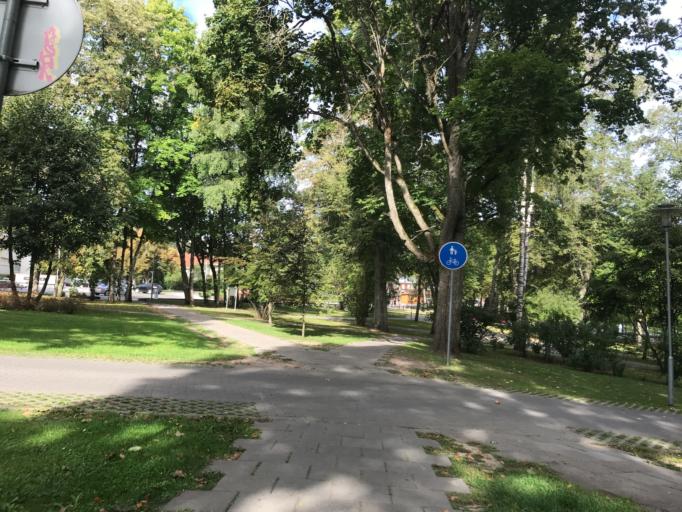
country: LT
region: Alytaus apskritis
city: Druskininkai
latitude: 54.0201
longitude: 23.9755
